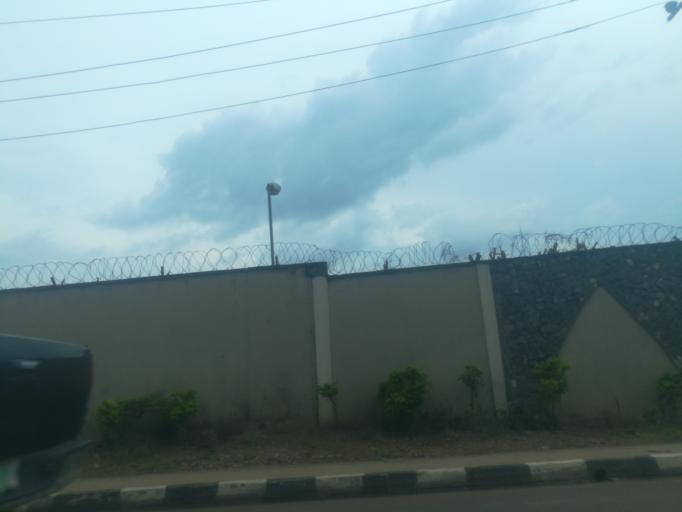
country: NG
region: Oyo
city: Ibadan
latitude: 7.3642
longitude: 3.8527
